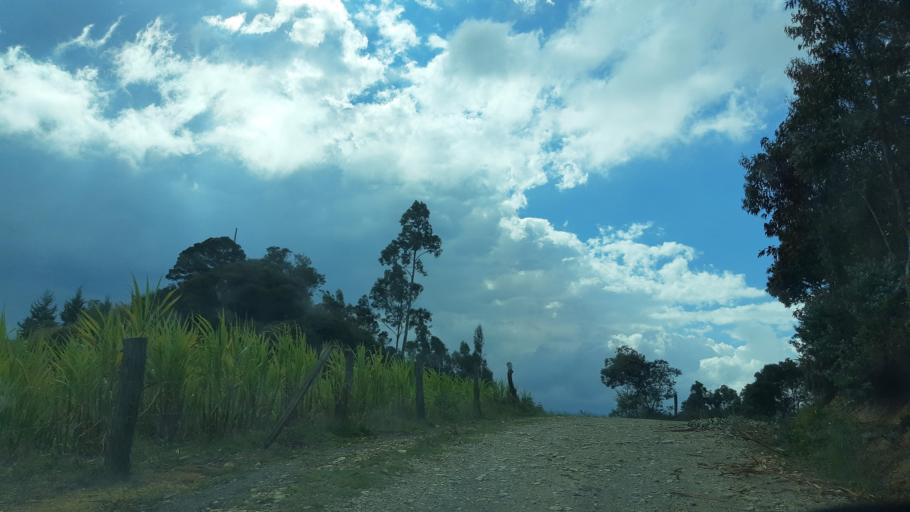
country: CO
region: Boyaca
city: Santa Sofia
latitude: 5.7262
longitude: -73.5516
